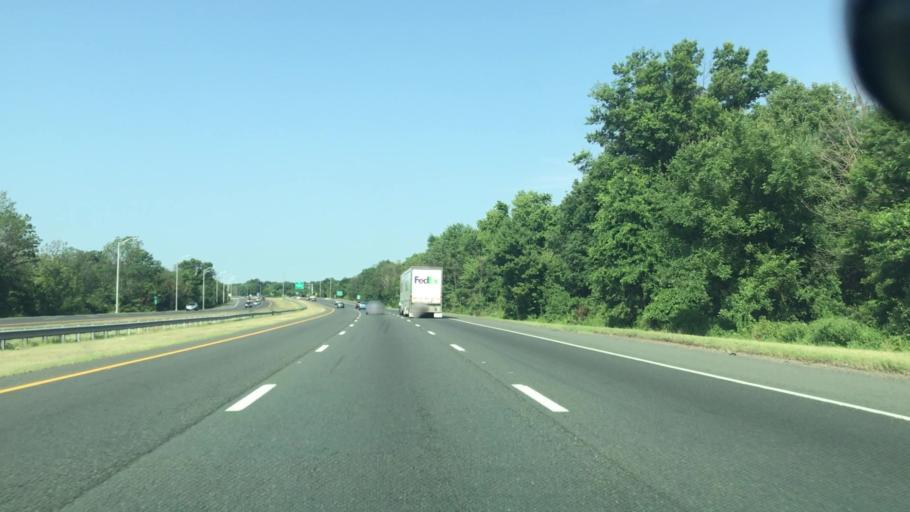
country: US
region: New Jersey
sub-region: Middlesex County
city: Middlesex
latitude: 40.5560
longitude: -74.4775
